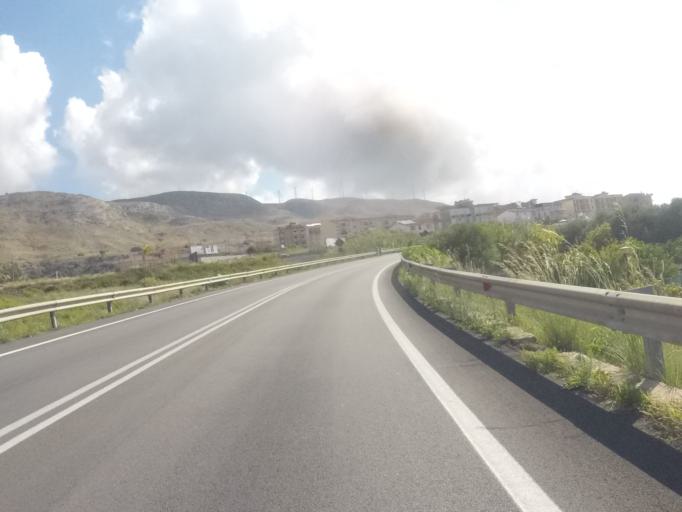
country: IT
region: Sicily
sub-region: Agrigento
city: Siculiana
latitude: 37.3337
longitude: 13.4272
